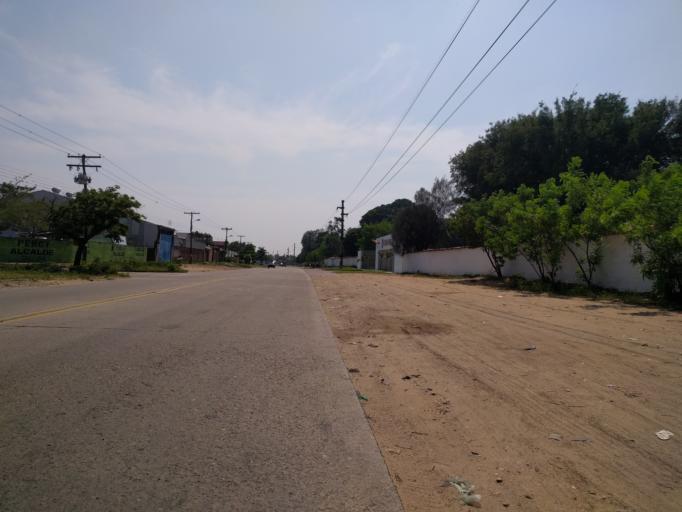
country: BO
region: Santa Cruz
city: Santa Cruz de la Sierra
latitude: -17.8028
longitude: -63.1631
